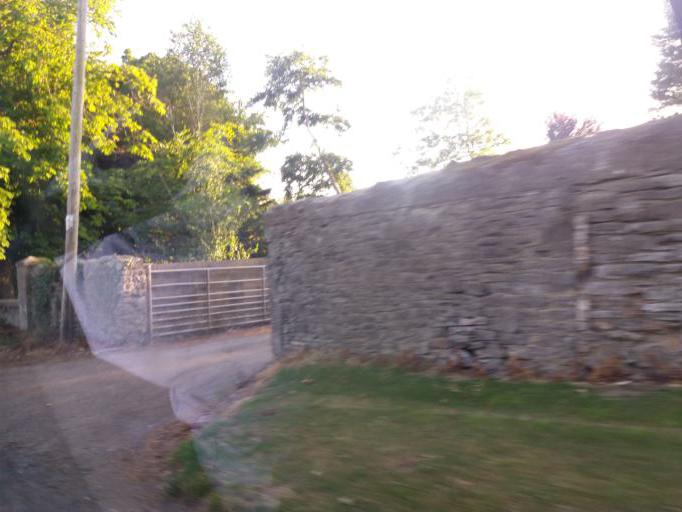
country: IE
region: Leinster
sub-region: An Mhi
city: Ashbourne
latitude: 53.5625
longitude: -6.3554
